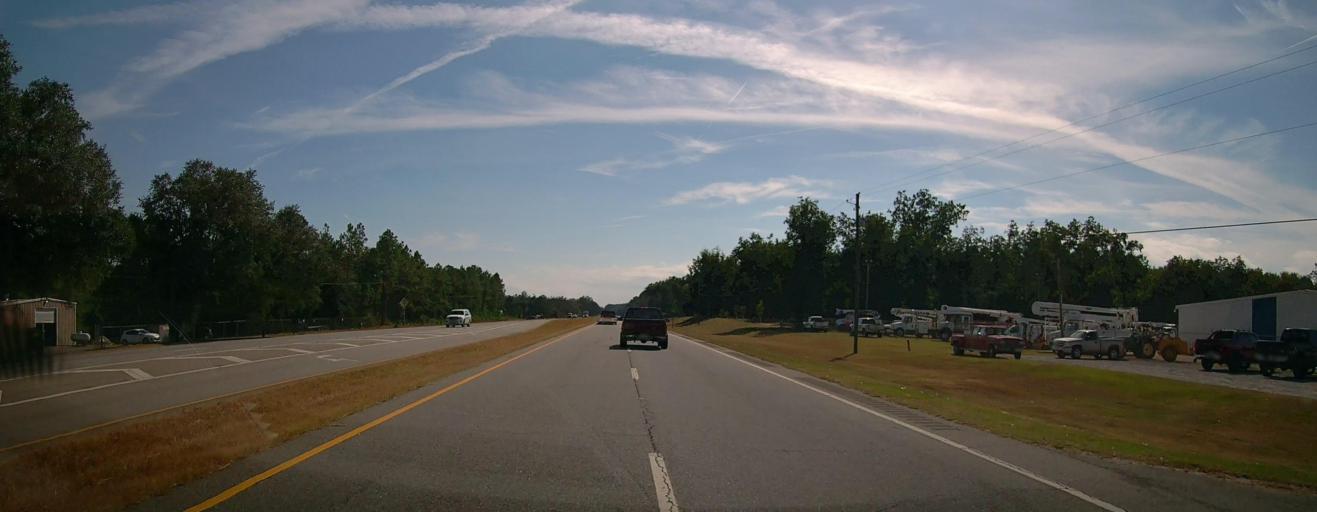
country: US
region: Georgia
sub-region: Dougherty County
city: Putney
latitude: 31.4829
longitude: -84.1168
